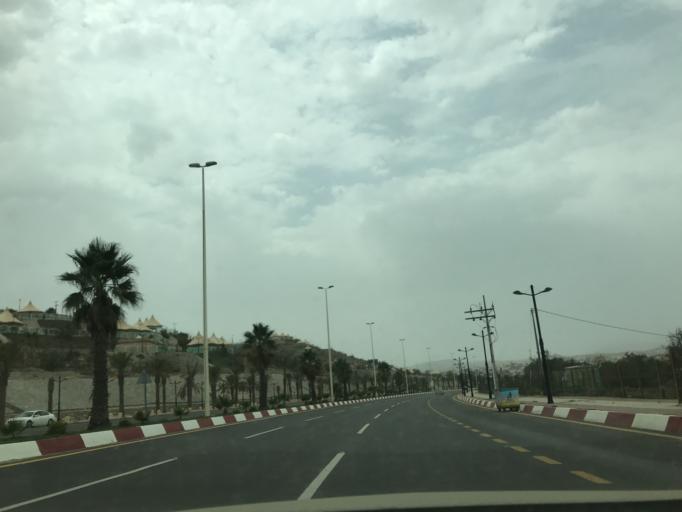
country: SA
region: Mintaqat al Bahah
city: Al Bahah
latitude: 19.8434
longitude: 41.5879
